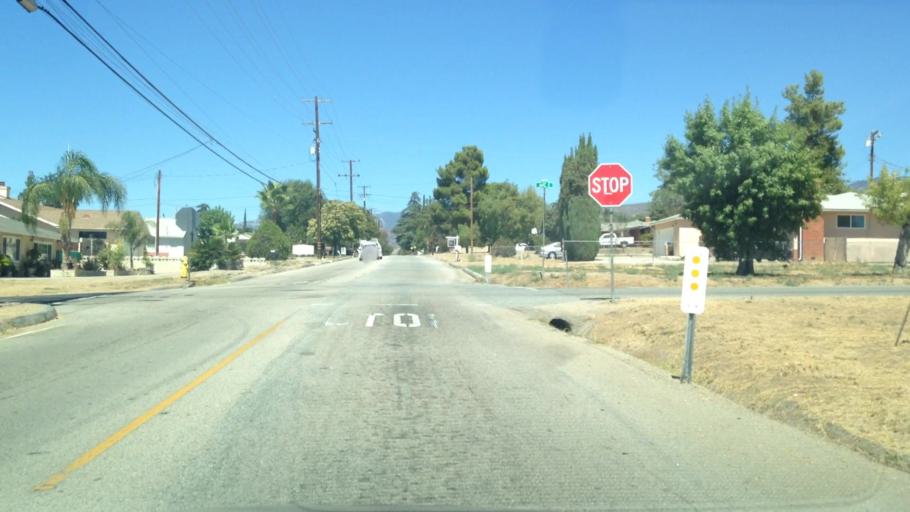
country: US
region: California
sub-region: San Bernardino County
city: Yucaipa
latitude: 34.0264
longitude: -117.0345
